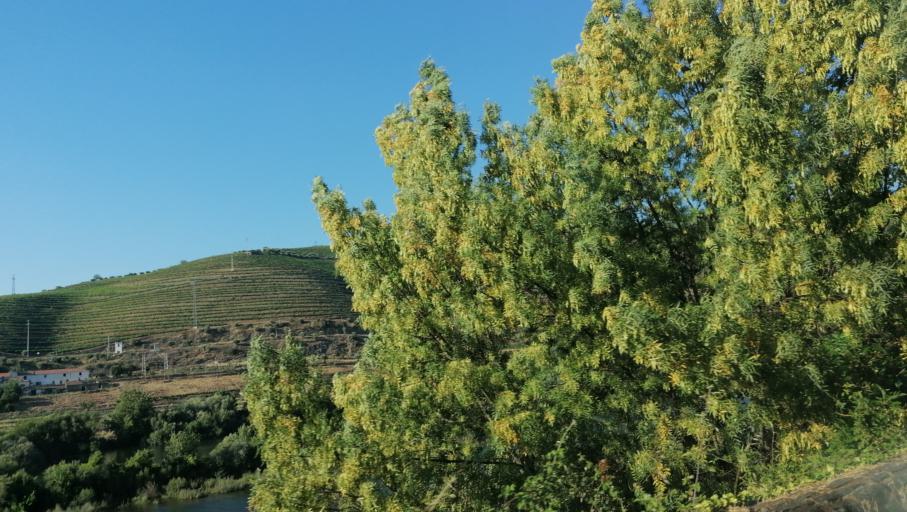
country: PT
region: Vila Real
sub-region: Peso da Regua
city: Peso da Regua
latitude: 41.1516
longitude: -7.7693
